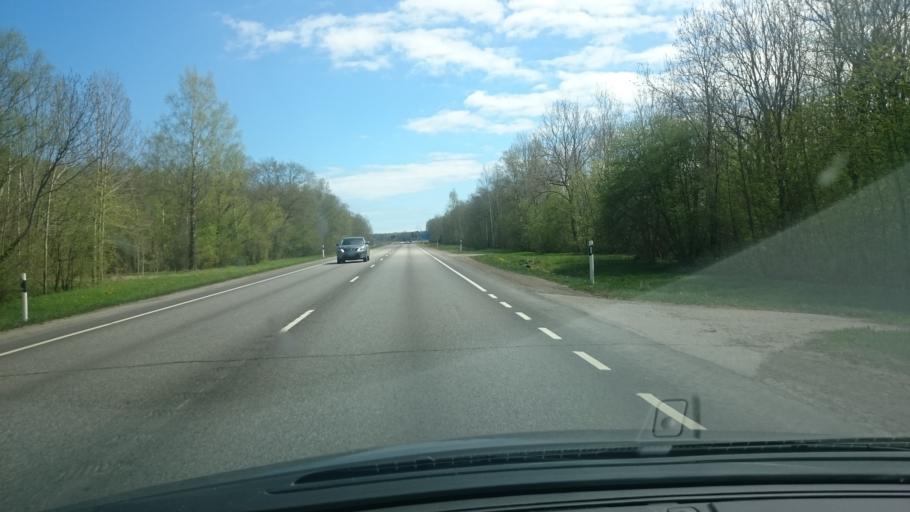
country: EE
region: Ida-Virumaa
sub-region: Kohtla-Jaerve linn
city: Kohtla-Jarve
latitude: 59.4207
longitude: 27.2628
